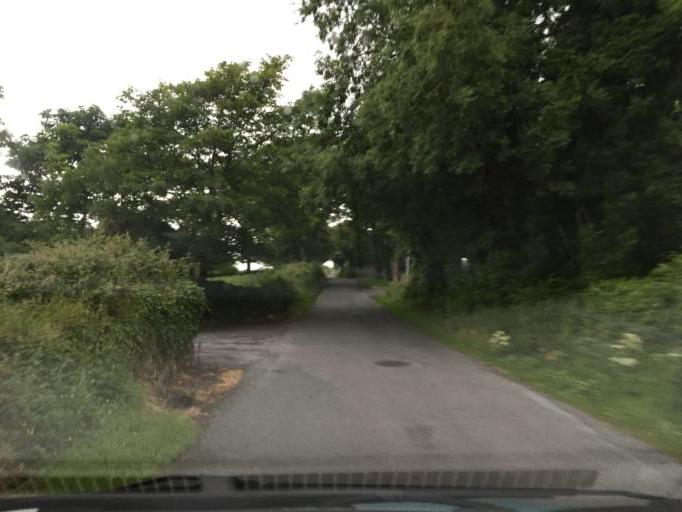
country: IE
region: Connaught
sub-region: Sligo
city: Strandhill
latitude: 54.2509
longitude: -8.5562
